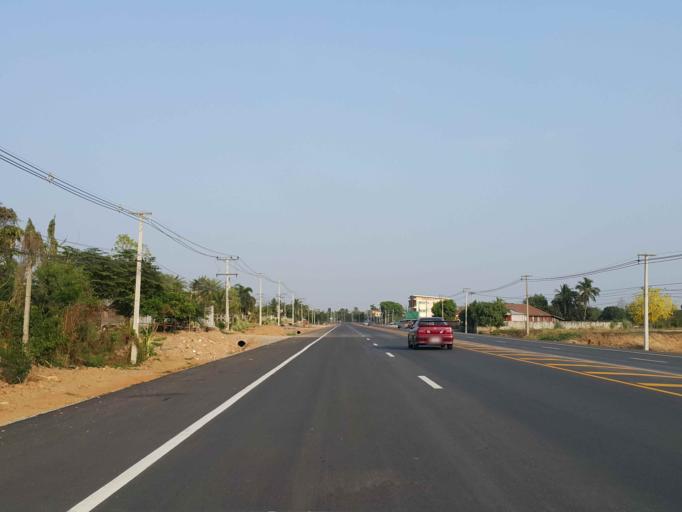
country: TH
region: Sukhothai
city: Sawankhalok
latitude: 17.3062
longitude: 99.8196
